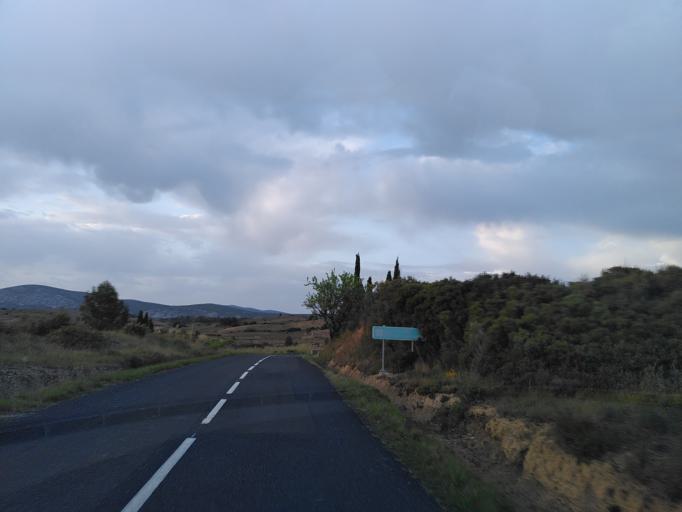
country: FR
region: Languedoc-Roussillon
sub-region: Departement des Pyrenees-Orientales
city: Estagel
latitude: 42.7994
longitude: 2.6975
